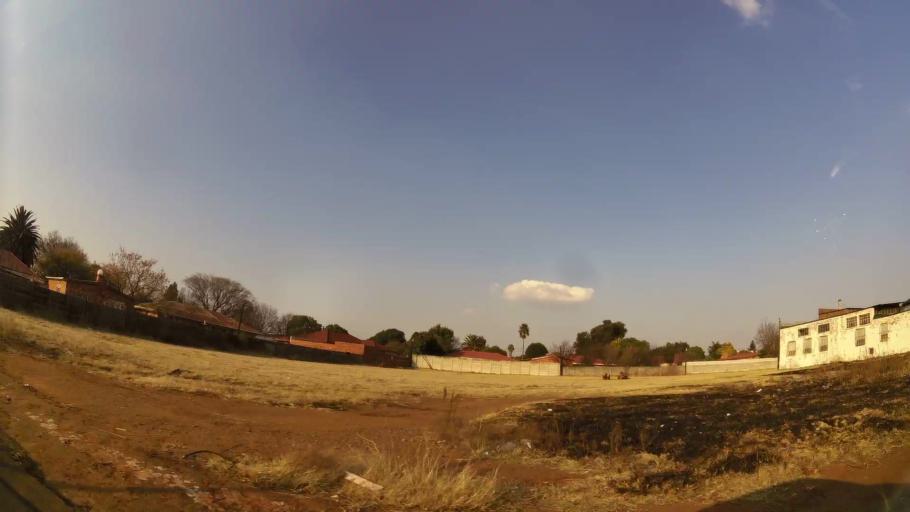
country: ZA
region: Gauteng
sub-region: Ekurhuleni Metropolitan Municipality
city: Springs
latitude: -26.2932
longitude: 28.4405
